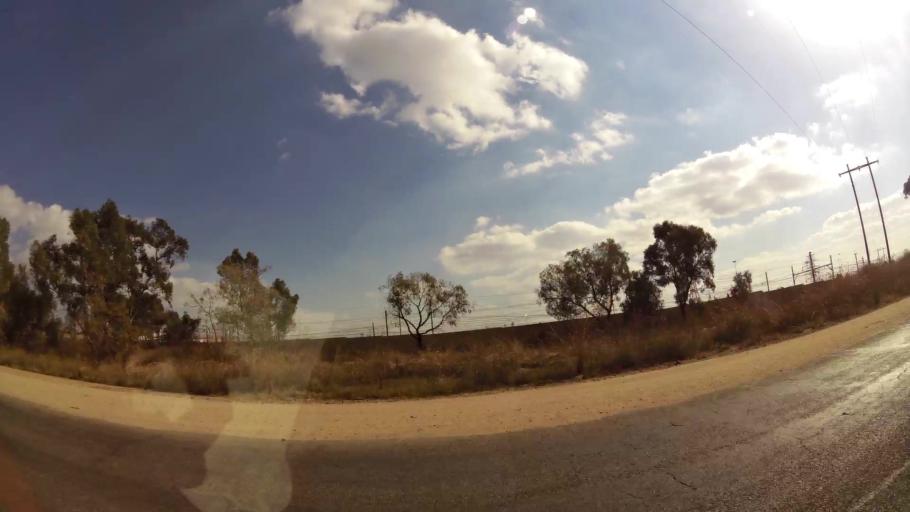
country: ZA
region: Gauteng
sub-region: Ekurhuleni Metropolitan Municipality
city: Tembisa
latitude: -26.0041
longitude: 28.2495
